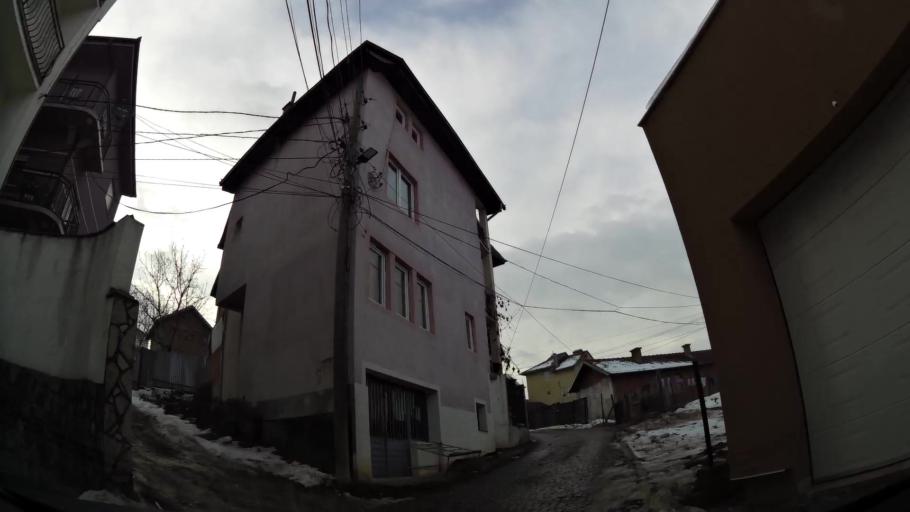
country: XK
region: Pristina
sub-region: Komuna e Prishtines
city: Pristina
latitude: 42.6627
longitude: 21.1710
